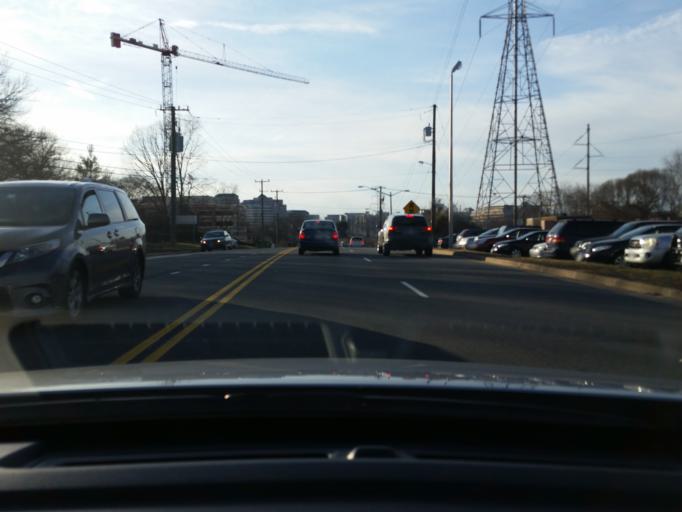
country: US
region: Virginia
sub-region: Fairfax County
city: Reston
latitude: 38.9505
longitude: -77.3375
